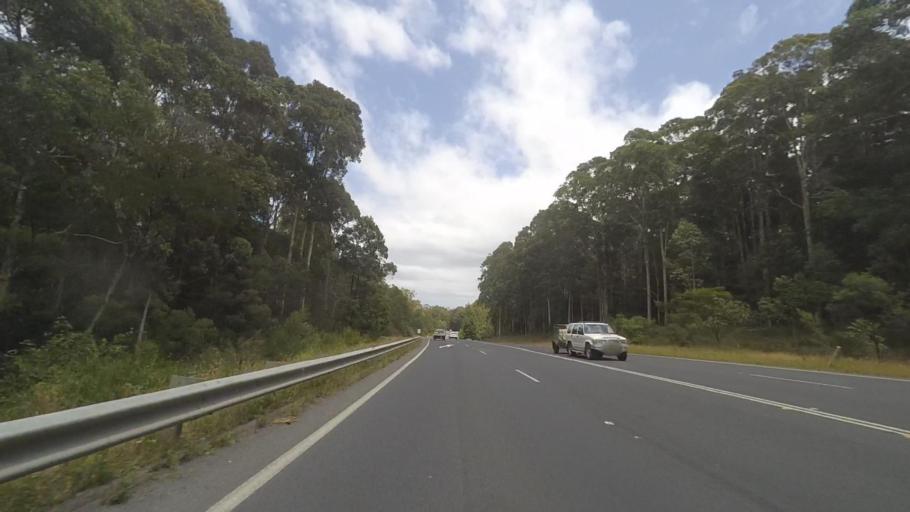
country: AU
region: New South Wales
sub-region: Shoalhaven Shire
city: Falls Creek
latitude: -35.0747
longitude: 150.5609
